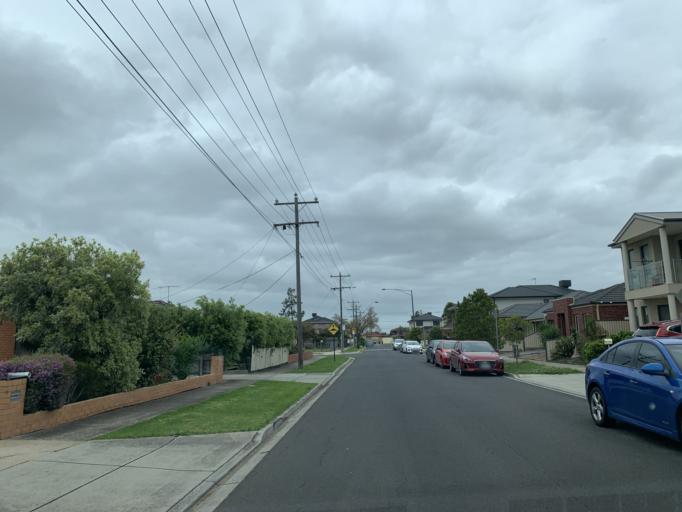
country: AU
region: Victoria
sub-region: Brimbank
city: St Albans
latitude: -37.7573
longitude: 144.8006
